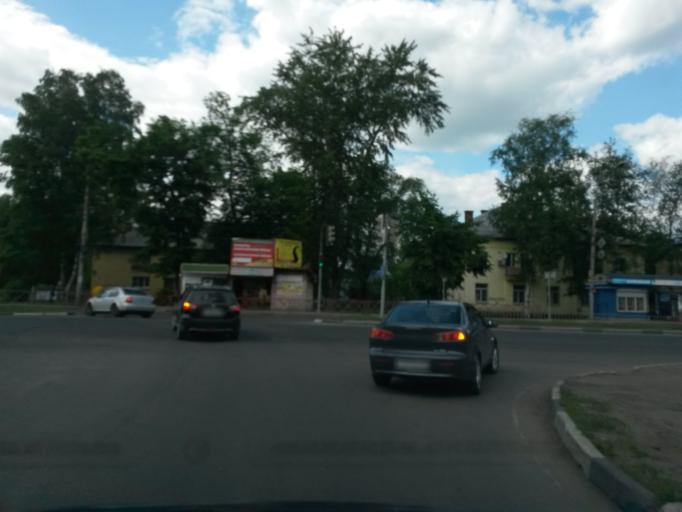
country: RU
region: Jaroslavl
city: Yaroslavl
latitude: 57.6522
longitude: 39.9354
